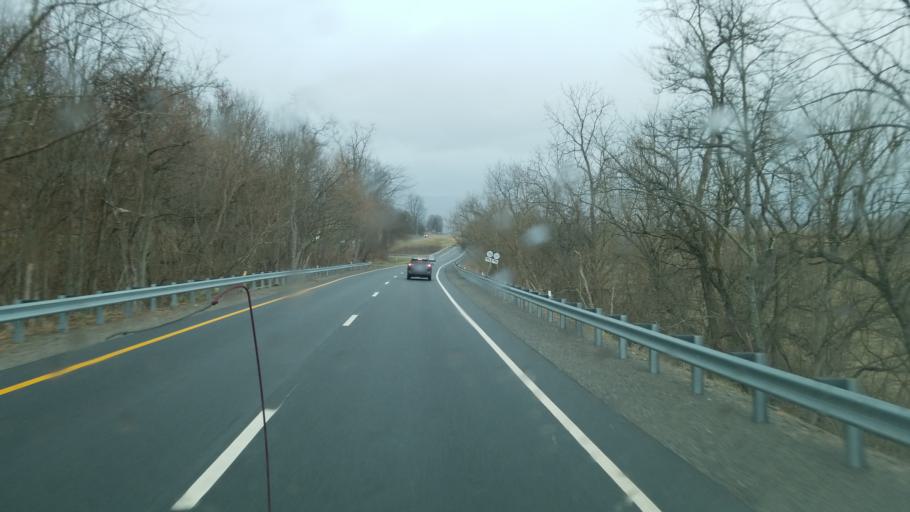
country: US
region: Virginia
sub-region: Giles County
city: Pearisburg
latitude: 37.3026
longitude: -80.7384
